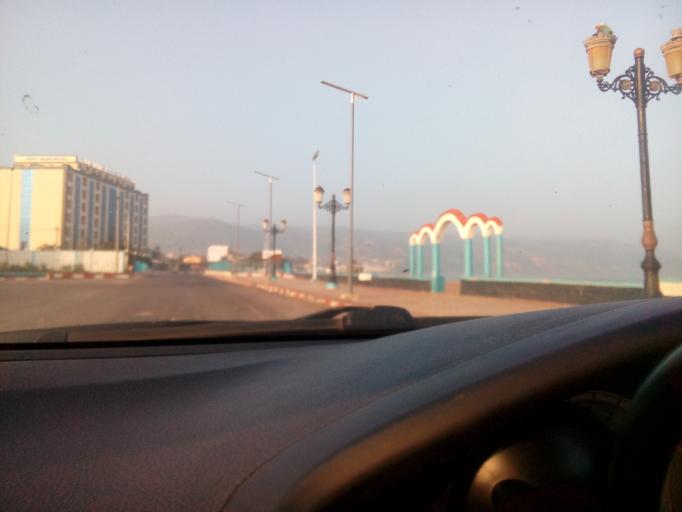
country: DZ
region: Oran
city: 'Ain el Turk
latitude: 35.7065
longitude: -0.8845
